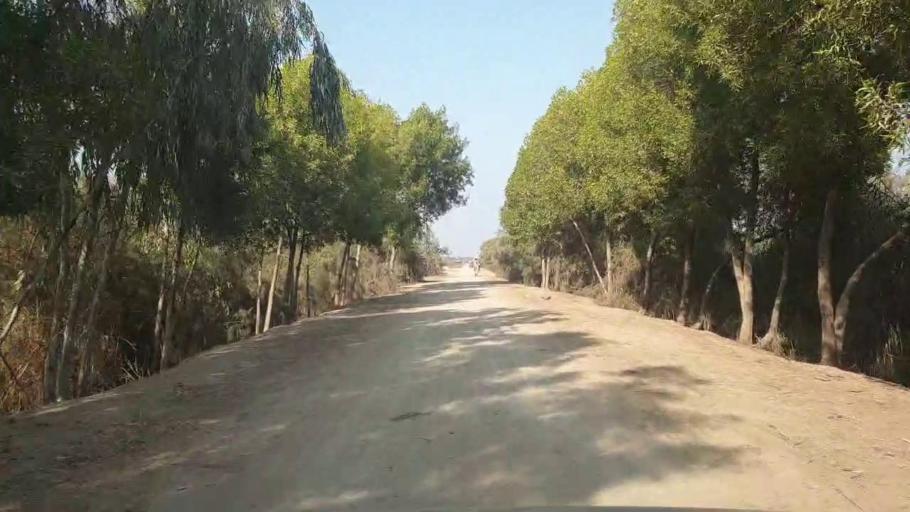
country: PK
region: Sindh
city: Tando Adam
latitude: 25.7984
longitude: 68.5923
